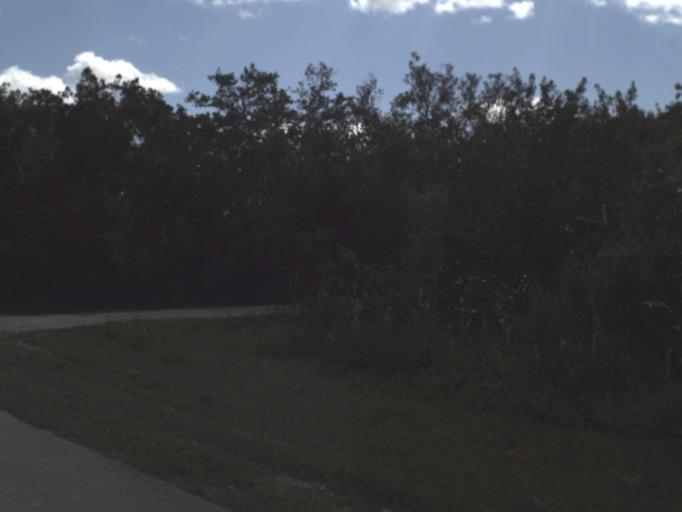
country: US
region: Florida
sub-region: Collier County
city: Marco
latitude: 25.9745
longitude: -81.5539
